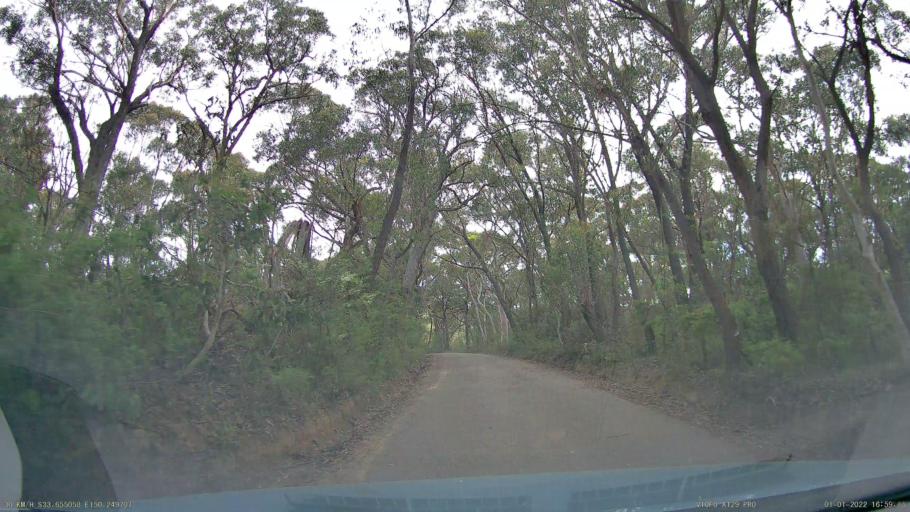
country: AU
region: New South Wales
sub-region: Blue Mountains Municipality
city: Blackheath
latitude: -33.6551
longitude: 150.2497
